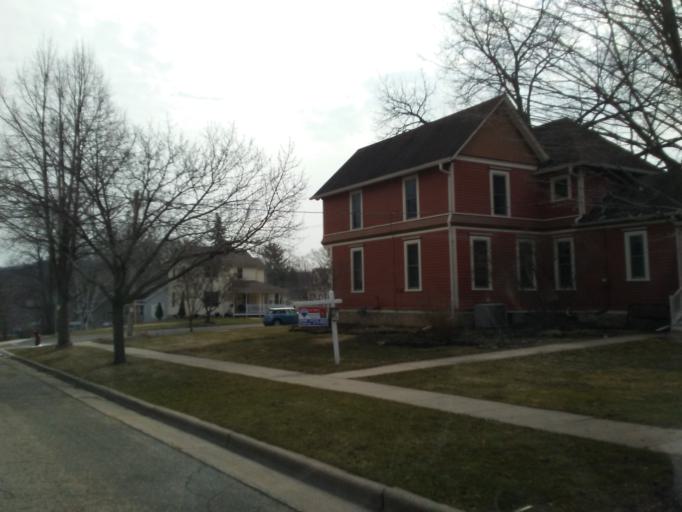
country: US
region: Wisconsin
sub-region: Columbia County
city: Lodi
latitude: 43.3125
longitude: -89.5328
